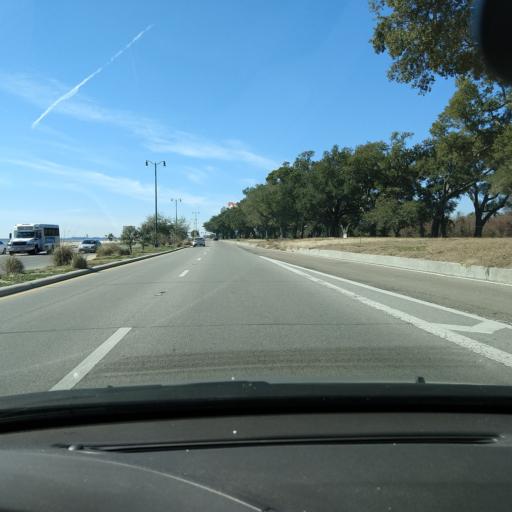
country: US
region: Mississippi
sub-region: Harrison County
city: Gulfport
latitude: 30.3834
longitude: -89.0226
